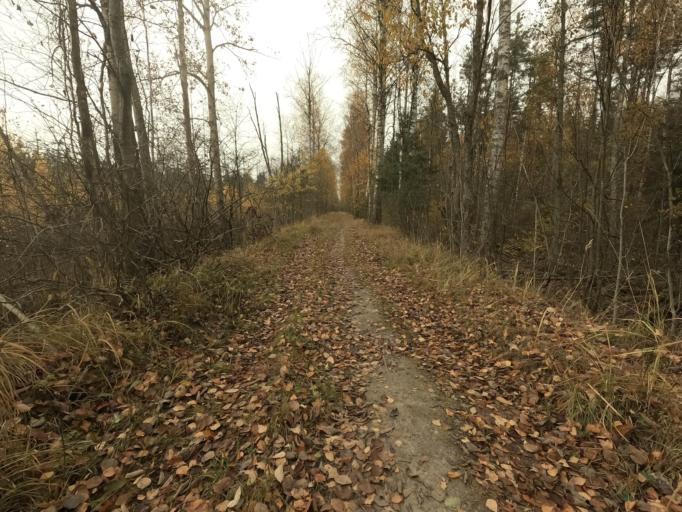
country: RU
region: Leningrad
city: Pavlovo
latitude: 59.7937
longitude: 30.8807
